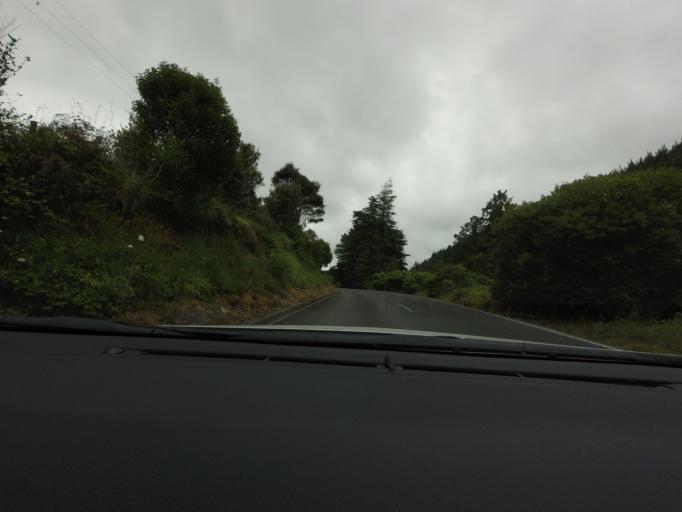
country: NZ
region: Auckland
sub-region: Auckland
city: Warkworth
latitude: -36.4681
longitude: 174.5491
